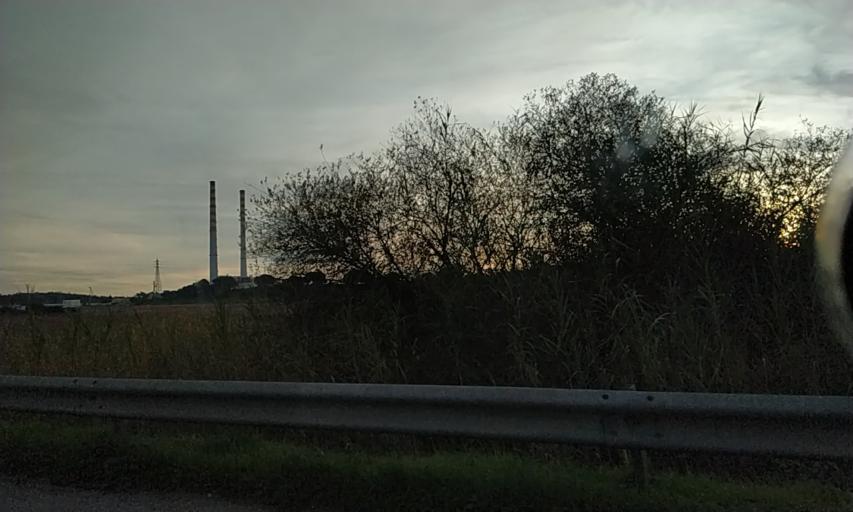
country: PT
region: Setubal
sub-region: Setubal
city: Setubal
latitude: 38.5205
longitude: -8.8412
